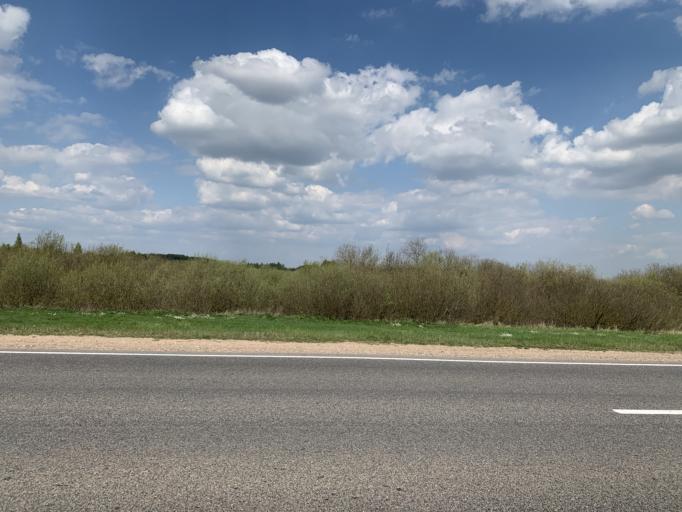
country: BY
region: Minsk
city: Nyasvizh
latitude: 53.2426
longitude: 26.7063
